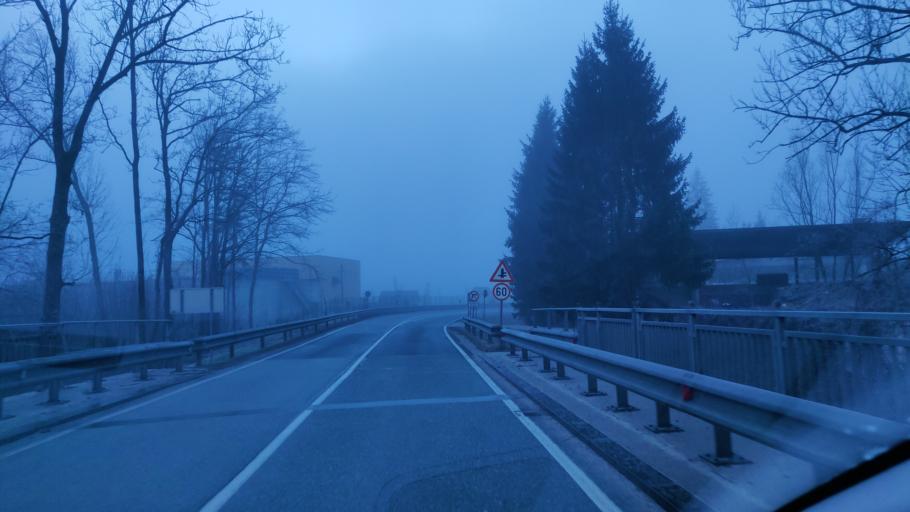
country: SI
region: Bohinj
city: Bohinjska Bistrica
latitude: 46.2796
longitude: 13.9529
